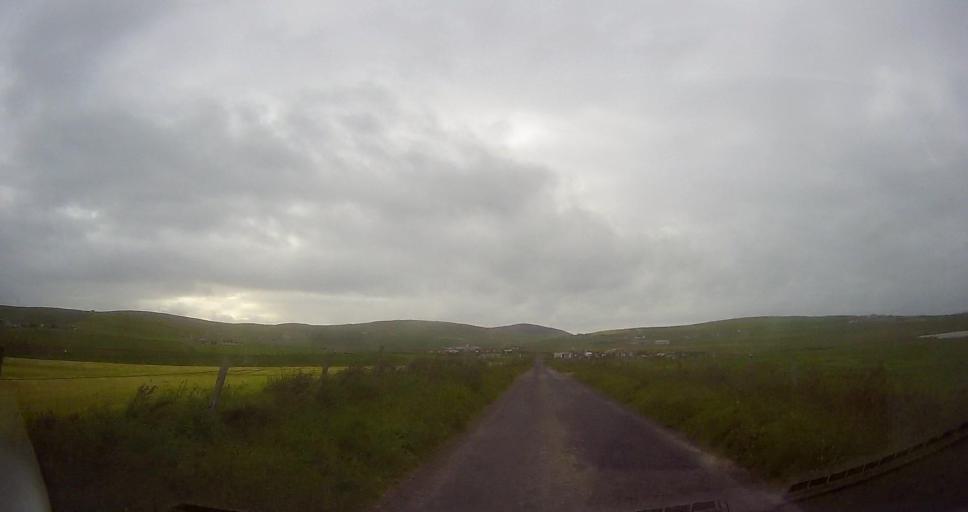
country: GB
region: Scotland
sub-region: Orkney Islands
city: Stromness
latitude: 58.9875
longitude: -3.2778
